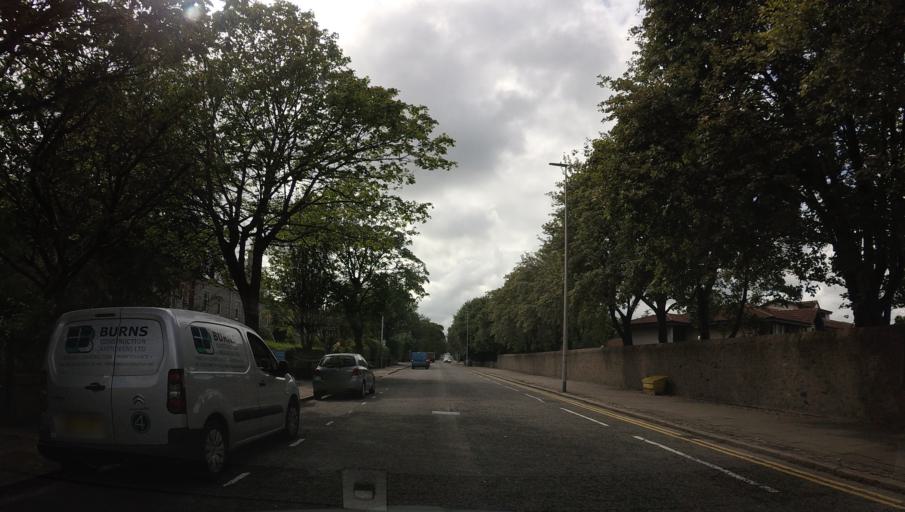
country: GB
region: Scotland
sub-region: Aberdeen City
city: Aberdeen
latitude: 57.1530
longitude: -2.1164
